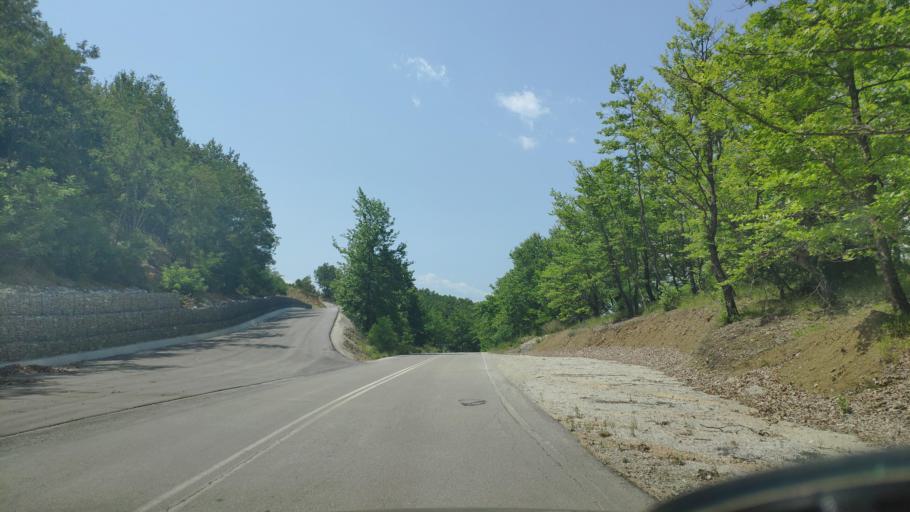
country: GR
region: Epirus
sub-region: Nomos Artas
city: Ano Kalentini
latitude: 39.2424
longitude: 21.1953
